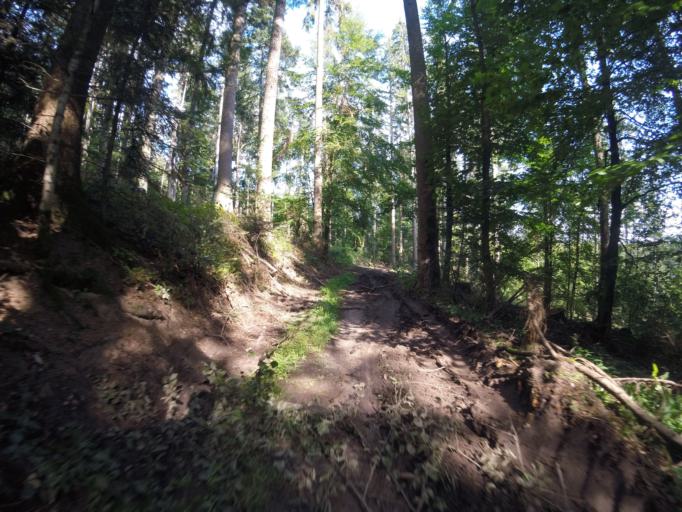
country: DE
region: Baden-Wuerttemberg
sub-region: Regierungsbezirk Stuttgart
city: Sulzbach an der Murr
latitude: 48.9699
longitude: 9.5236
